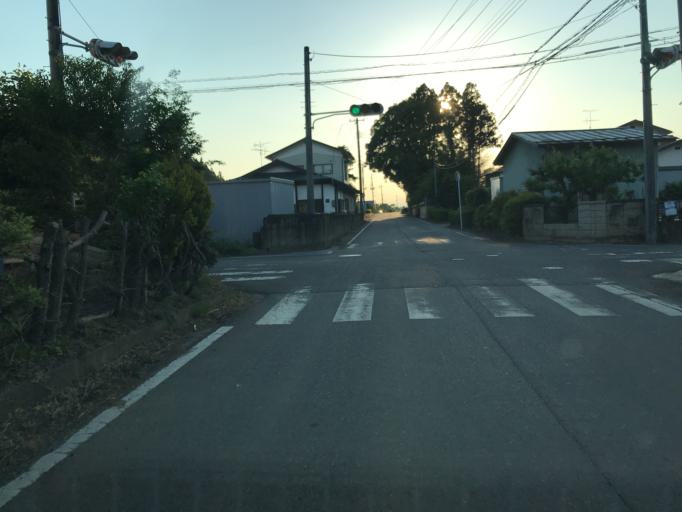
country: JP
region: Fukushima
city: Ishikawa
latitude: 37.1757
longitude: 140.3472
